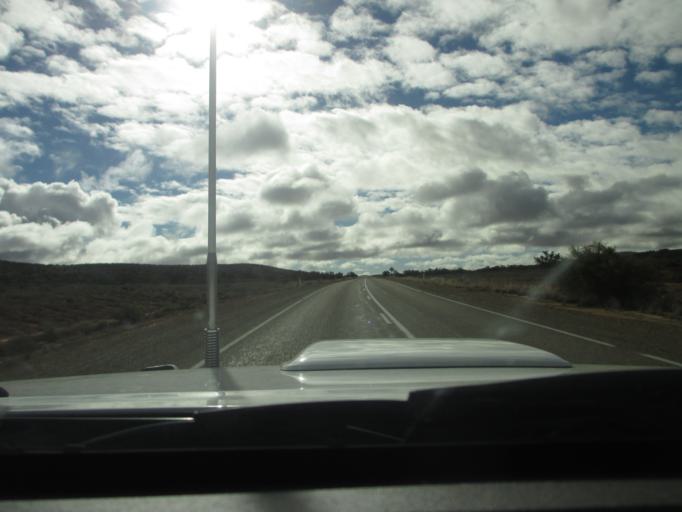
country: AU
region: South Australia
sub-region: Flinders Ranges
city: Quorn
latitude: -32.2081
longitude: 138.5243
